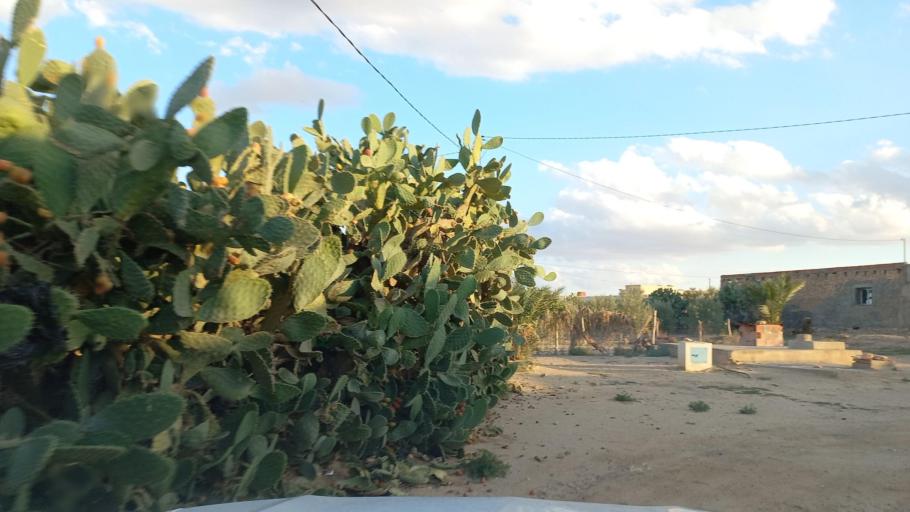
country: TN
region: Al Qasrayn
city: Sbiba
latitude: 35.3800
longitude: 9.0510
